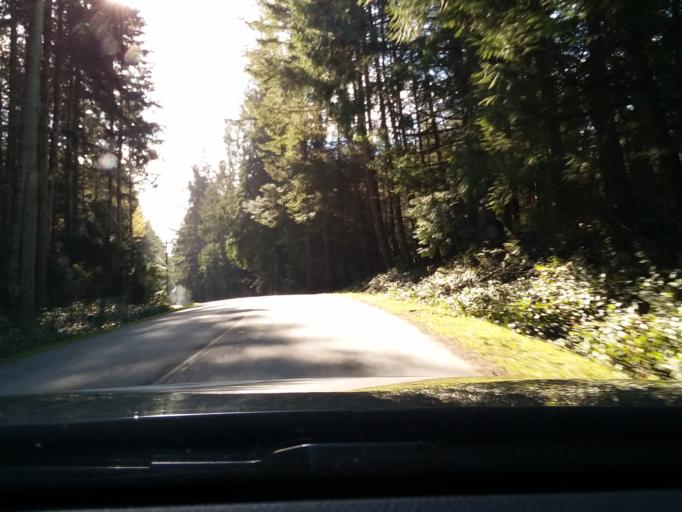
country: CA
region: British Columbia
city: North Saanich
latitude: 48.9194
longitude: -123.4372
